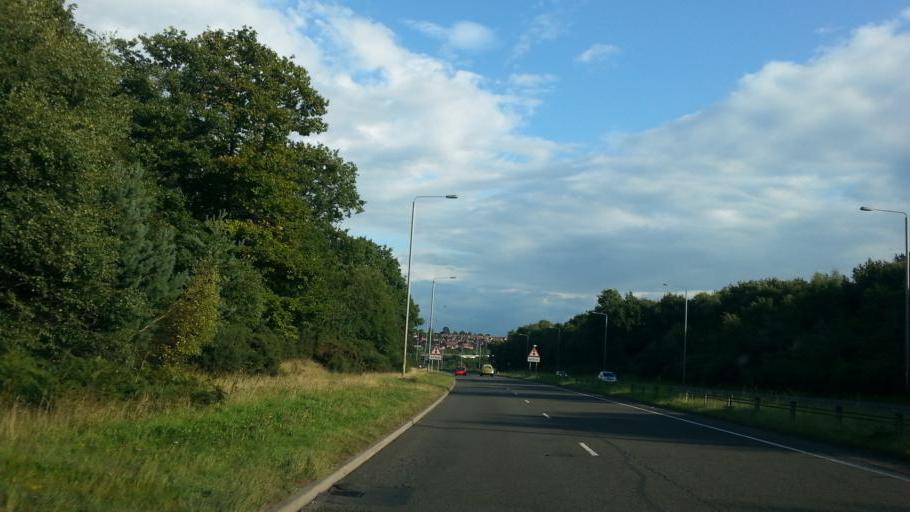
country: GB
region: England
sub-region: Nottinghamshire
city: Rainworth
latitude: 53.1252
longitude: -1.1224
